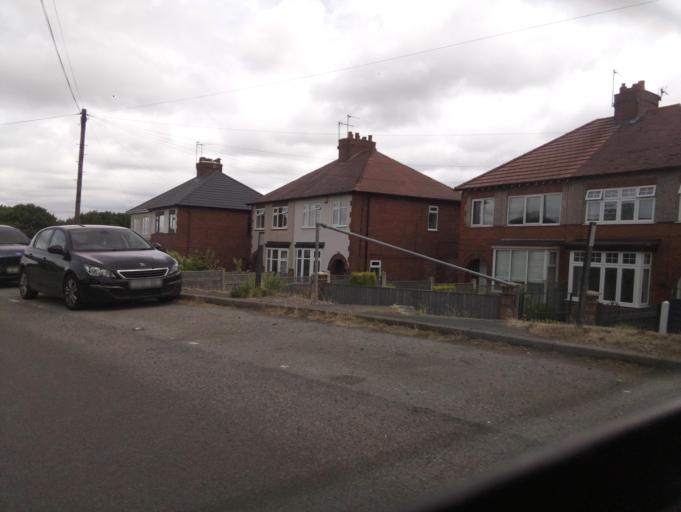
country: GB
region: England
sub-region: Derbyshire
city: Heanor
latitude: 53.0061
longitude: -1.3800
